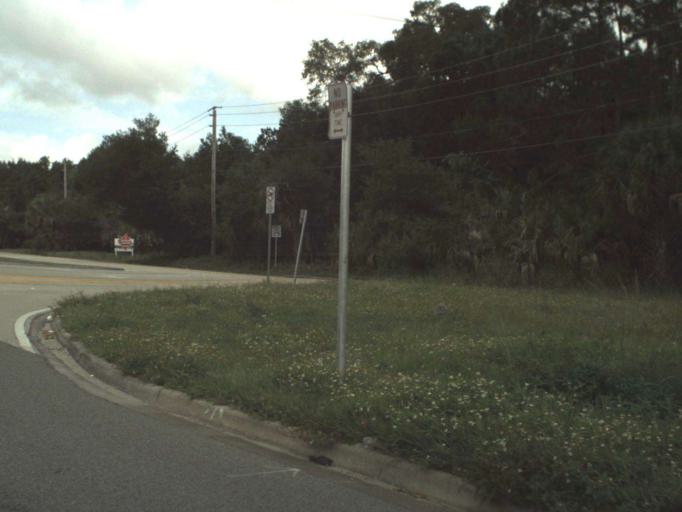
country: US
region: Florida
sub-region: Seminole County
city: Sanford
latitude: 28.8114
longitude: -81.2913
